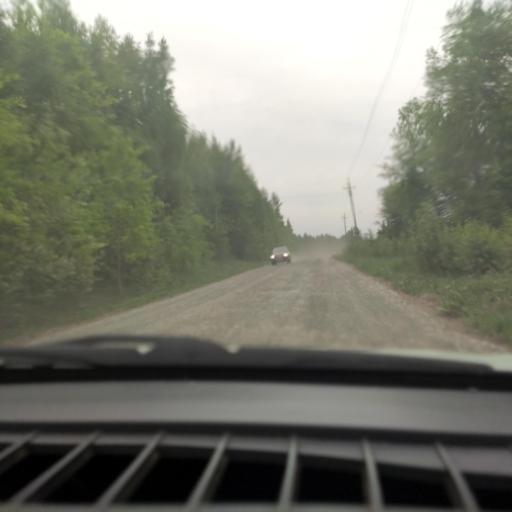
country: RU
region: Perm
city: Novyye Lyady
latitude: 57.9154
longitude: 56.6578
